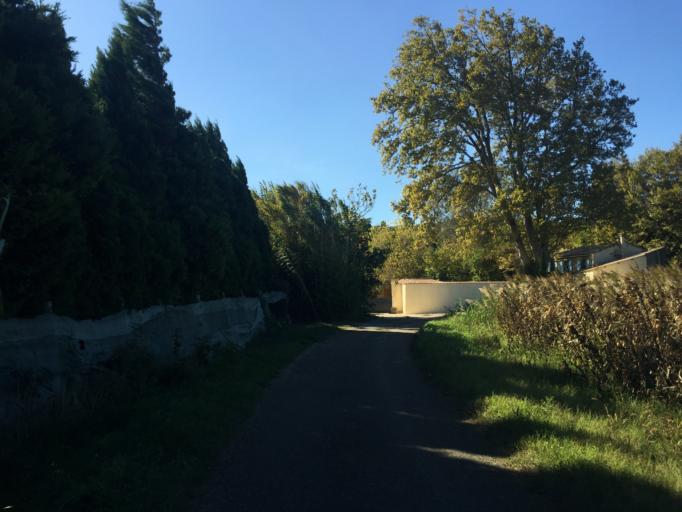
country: FR
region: Provence-Alpes-Cote d'Azur
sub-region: Departement du Vaucluse
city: Courthezon
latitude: 44.0931
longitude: 4.8568
